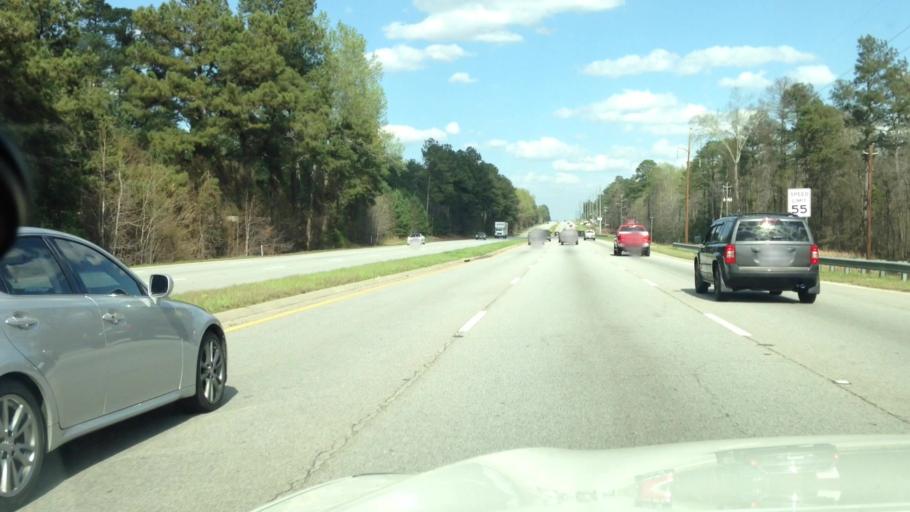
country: US
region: Georgia
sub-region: Columbia County
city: Martinez
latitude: 33.4405
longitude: -82.1070
